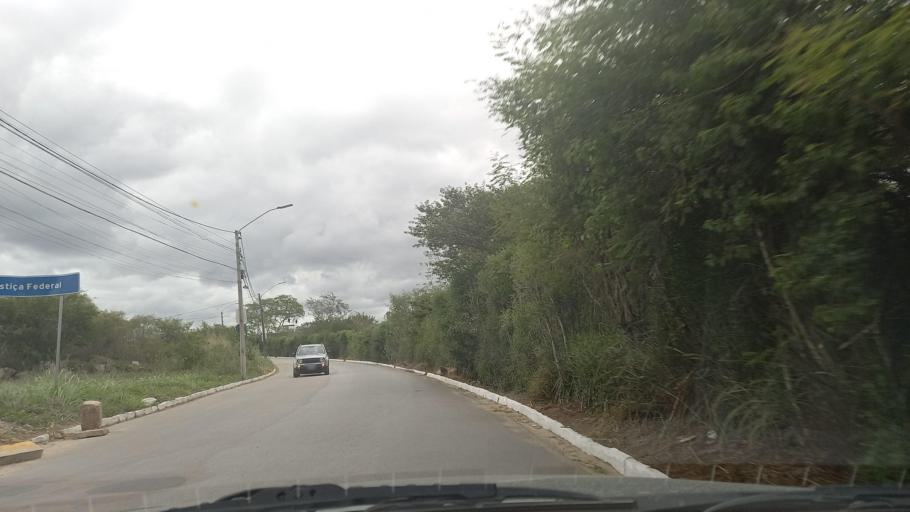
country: BR
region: Pernambuco
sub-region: Caruaru
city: Caruaru
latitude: -8.2575
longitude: -35.9657
